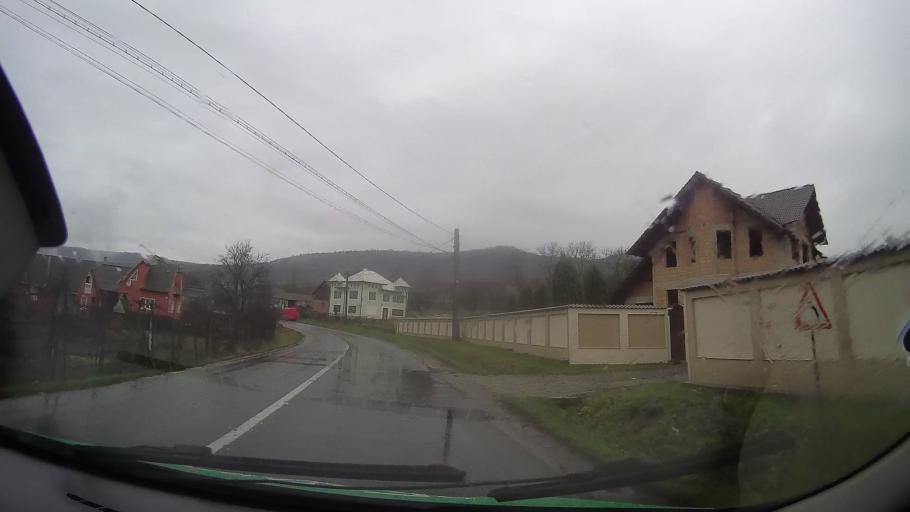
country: RO
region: Bistrita-Nasaud
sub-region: Comuna Mariselu
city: Mariselu
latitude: 47.0139
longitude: 24.5536
